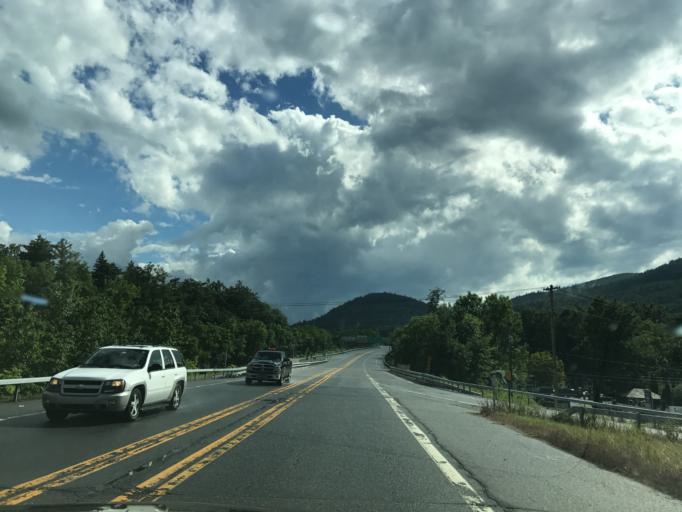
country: US
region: New York
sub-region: Warren County
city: Warrensburg
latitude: 43.4348
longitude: -73.7149
